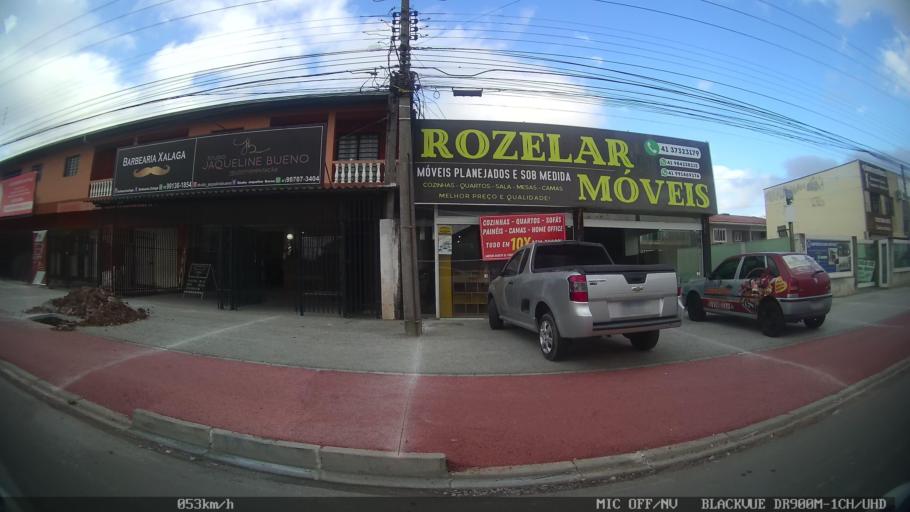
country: BR
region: Parana
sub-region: Pinhais
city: Pinhais
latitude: -25.4341
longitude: -49.1623
